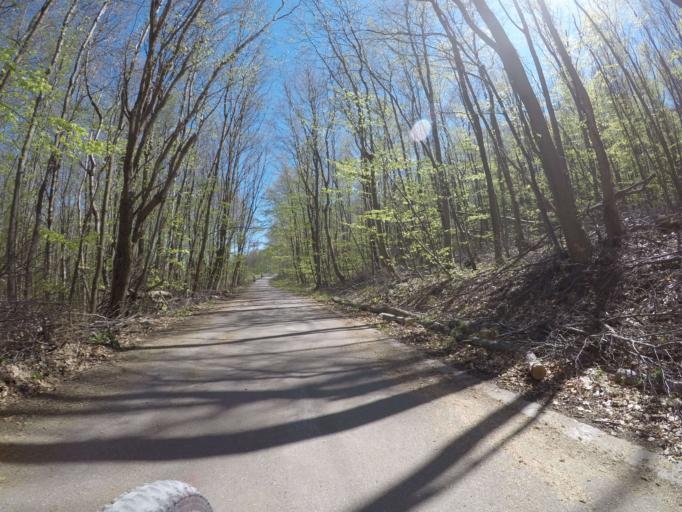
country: AT
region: Lower Austria
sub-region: Politischer Bezirk Modling
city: Gumpoldskirchen
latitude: 48.0539
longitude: 16.2467
